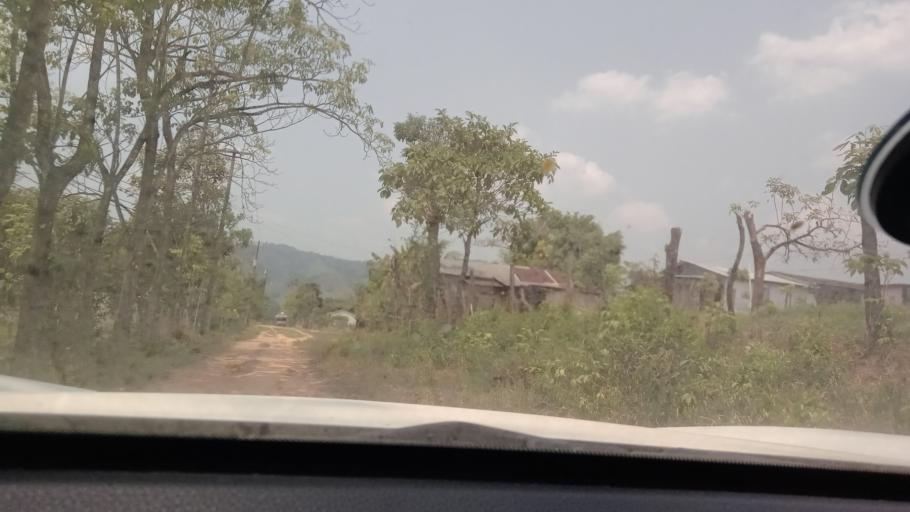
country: MX
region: Chiapas
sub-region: Tecpatan
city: Raudales Malpaso
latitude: 17.4696
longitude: -93.8251
